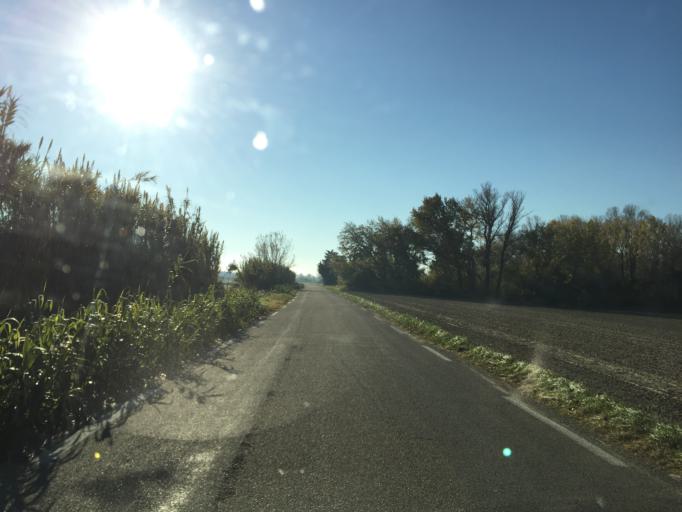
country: FR
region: Provence-Alpes-Cote d'Azur
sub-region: Departement du Vaucluse
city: Bedarrides
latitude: 44.0482
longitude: 4.9310
